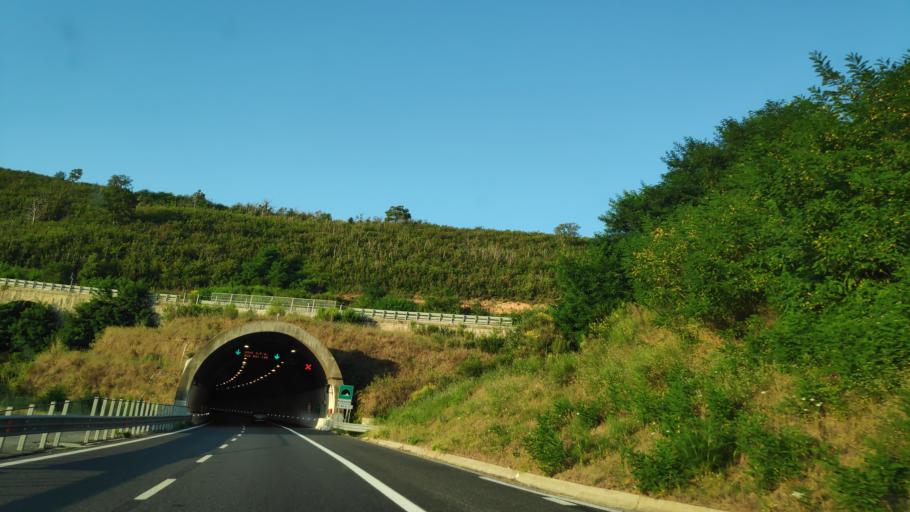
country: IT
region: Calabria
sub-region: Provincia di Reggio Calabria
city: Ceramida-Pellegrina
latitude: 38.2938
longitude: 15.8399
